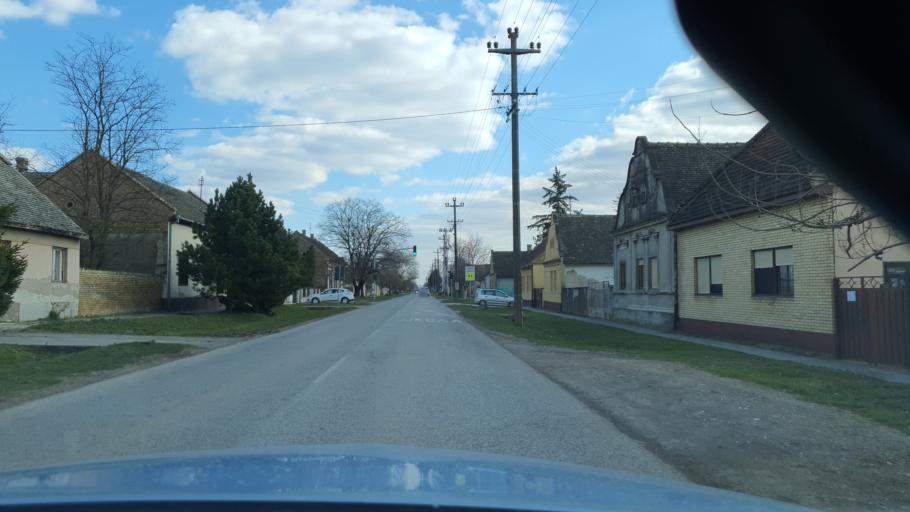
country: RS
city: Ravno Selo
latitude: 45.4500
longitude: 19.6196
